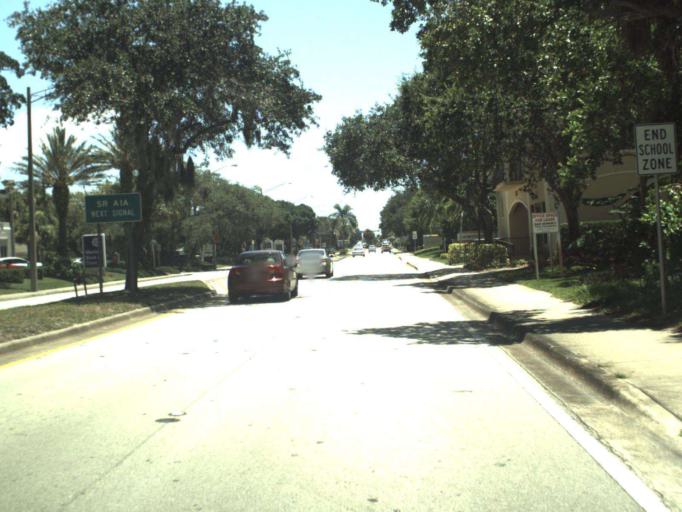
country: US
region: Florida
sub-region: Indian River County
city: Vero Beach
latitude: 27.6533
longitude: -80.3635
